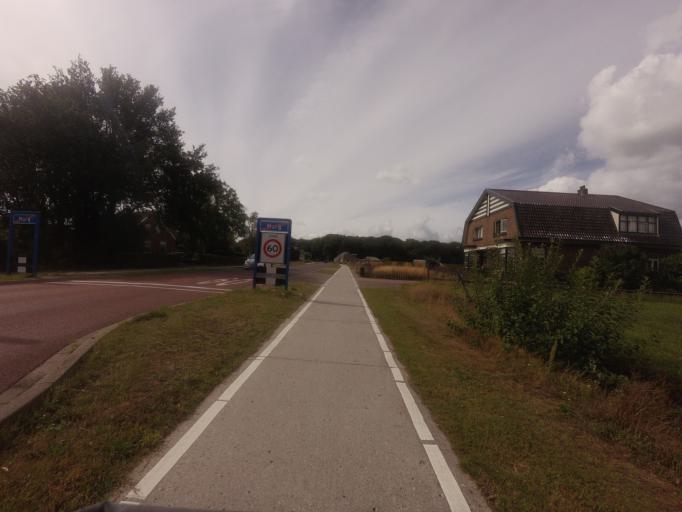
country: NL
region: Drenthe
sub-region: Gemeente Tynaarlo
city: Vries
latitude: 53.0604
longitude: 6.4573
